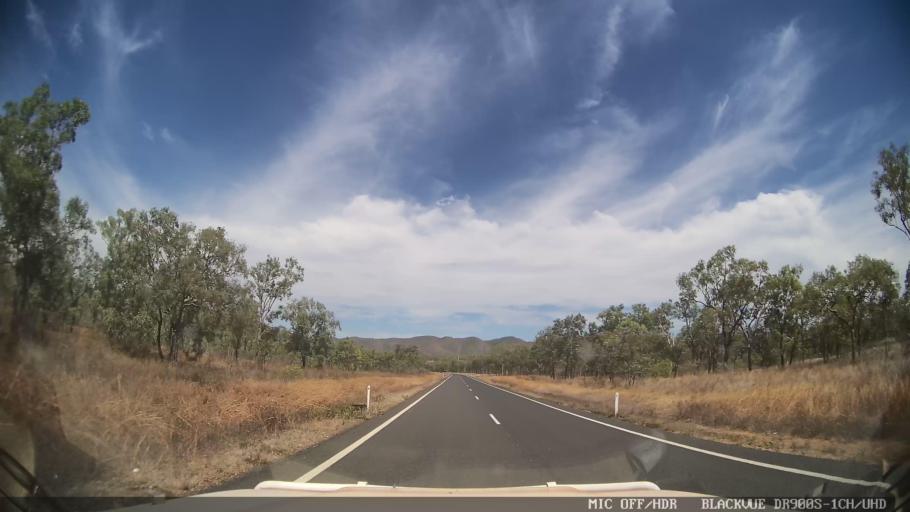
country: AU
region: Queensland
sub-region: Cook
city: Cooktown
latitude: -15.9329
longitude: 144.8400
